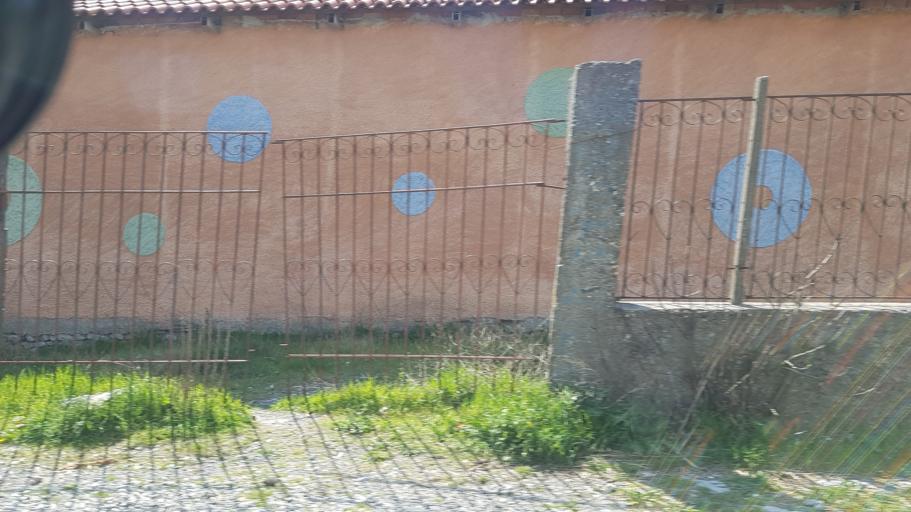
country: AL
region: Shkoder
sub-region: Rrethi i Shkodres
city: Guri i Zi
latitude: 42.0243
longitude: 19.5751
